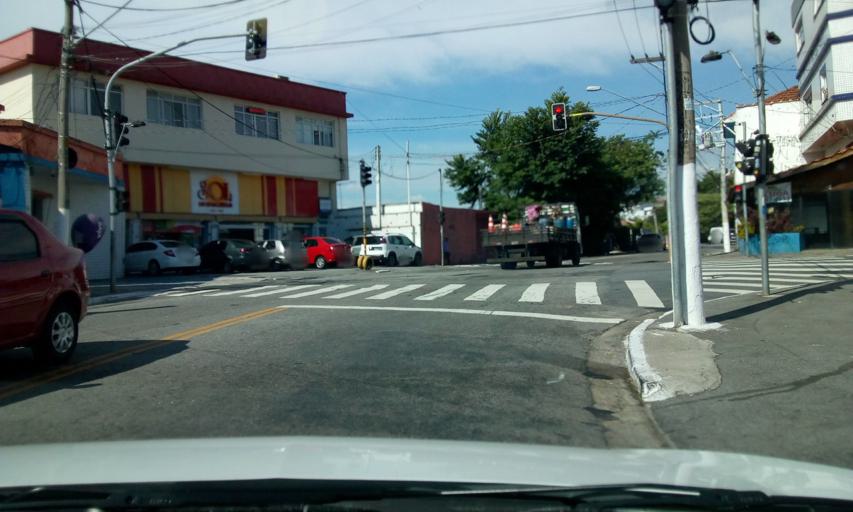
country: BR
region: Sao Paulo
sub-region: Sao Paulo
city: Sao Paulo
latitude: -23.5020
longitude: -46.6571
